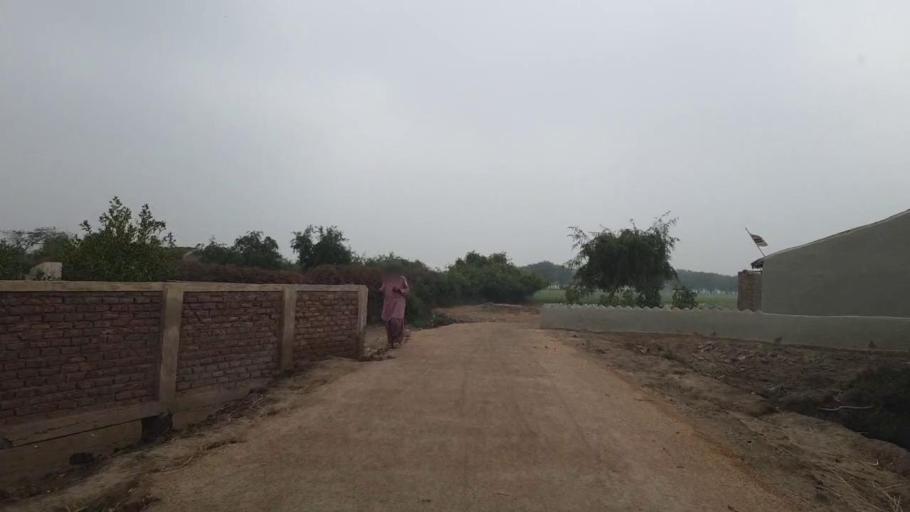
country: PK
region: Sindh
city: Badin
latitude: 24.5681
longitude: 68.6641
